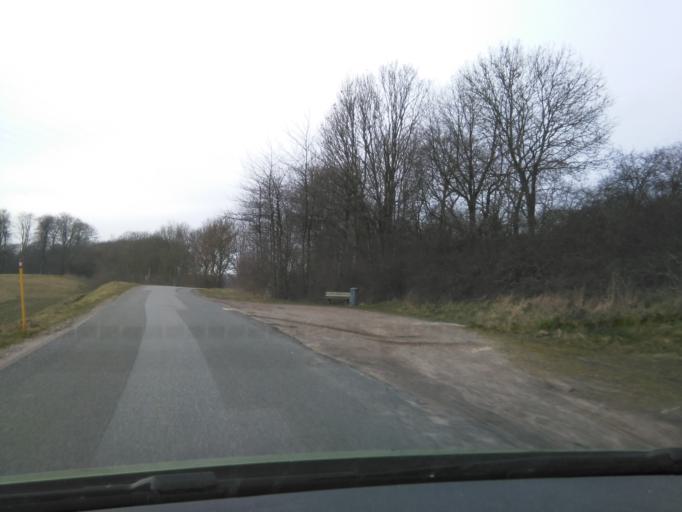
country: DK
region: Central Jutland
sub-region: Odder Kommune
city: Odder
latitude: 55.9305
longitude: 10.0930
